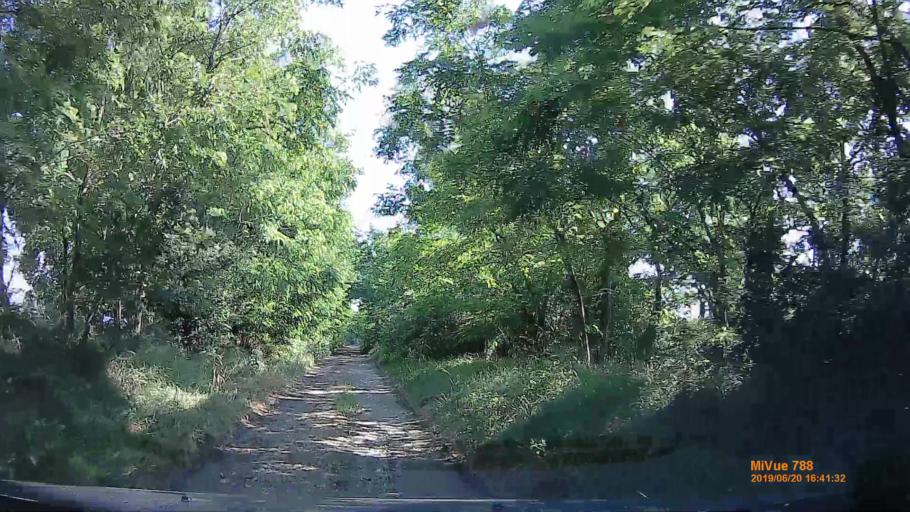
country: HU
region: Baranya
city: Buekkoesd
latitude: 46.1640
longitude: 18.0350
